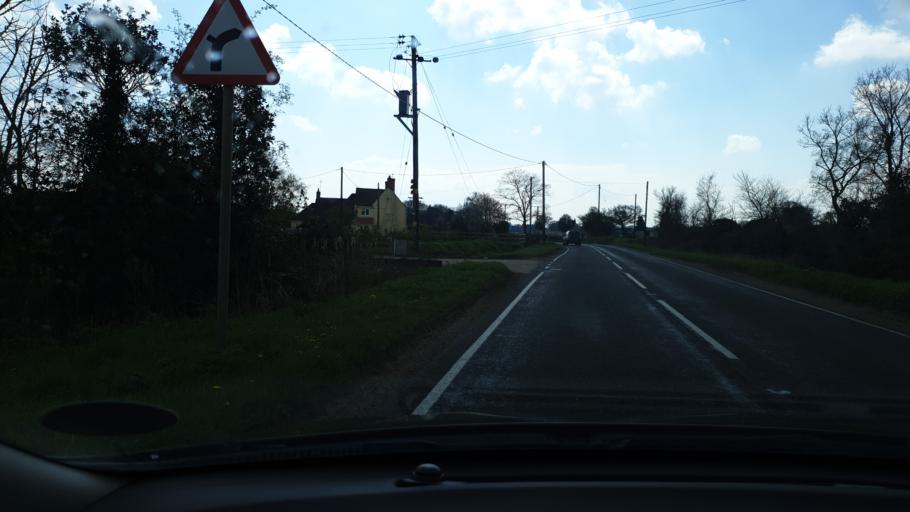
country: GB
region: England
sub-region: Essex
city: Great Bentley
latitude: 51.8598
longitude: 1.0369
